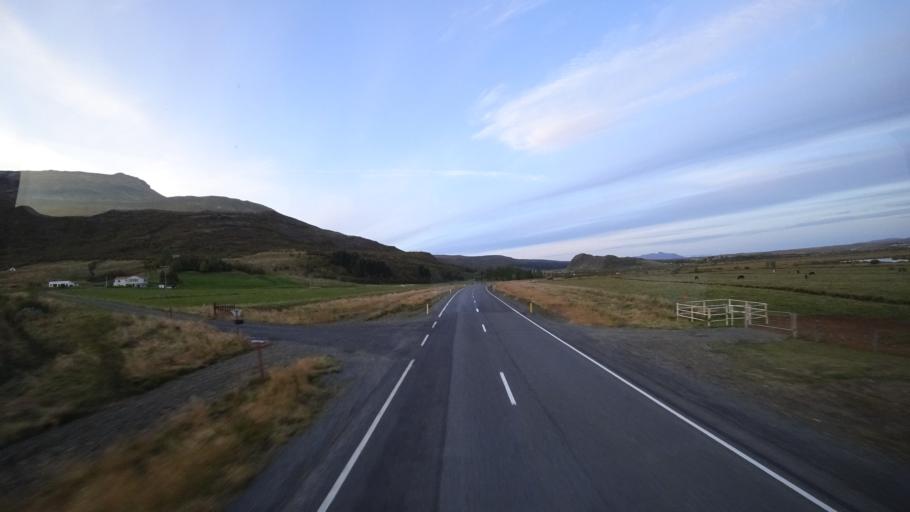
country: IS
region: South
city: Selfoss
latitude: 64.3006
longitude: -20.3309
